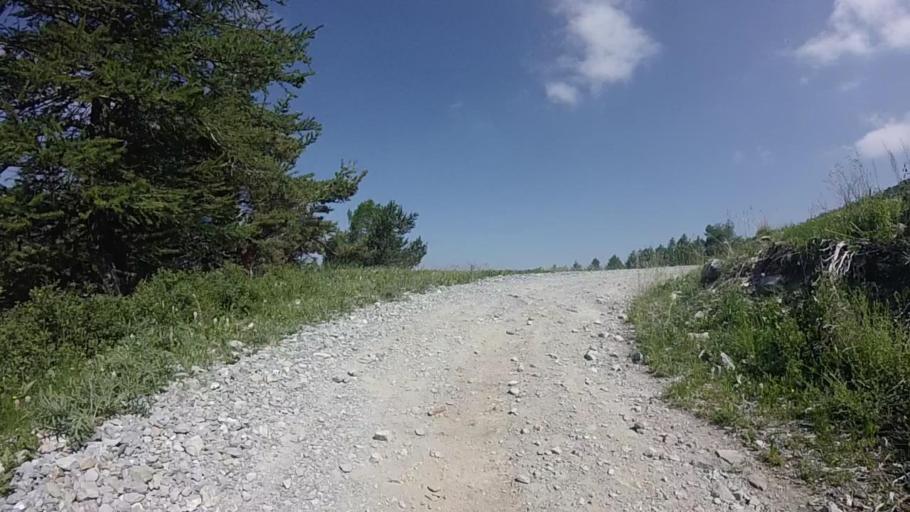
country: FR
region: Provence-Alpes-Cote d'Azur
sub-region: Departement des Alpes-de-Haute-Provence
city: Seyne-les-Alpes
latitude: 44.4060
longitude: 6.3677
